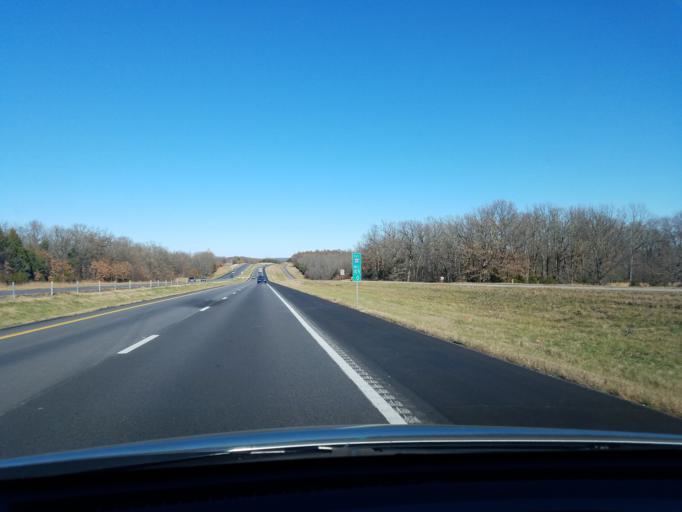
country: US
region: Missouri
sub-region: Webster County
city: Marshfield
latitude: 37.3926
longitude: -92.8992
